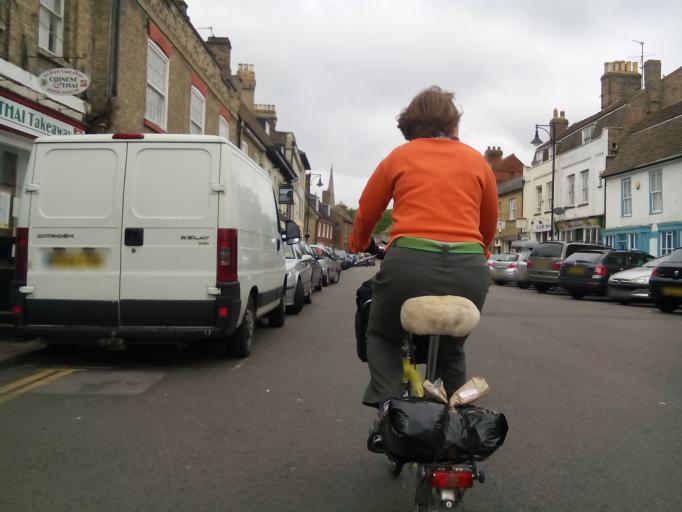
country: GB
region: England
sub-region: Cambridgeshire
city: Hemingford Grey
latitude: 52.3245
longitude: -0.0759
